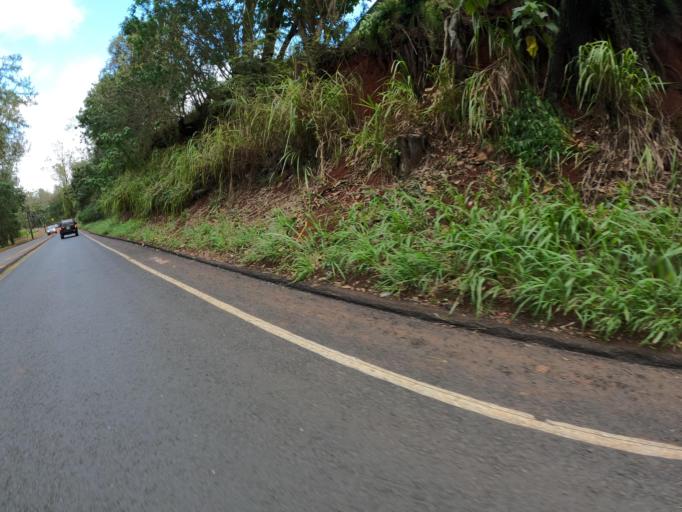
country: US
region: Hawaii
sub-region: Honolulu County
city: Wahiawa
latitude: 21.4990
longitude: -158.0294
